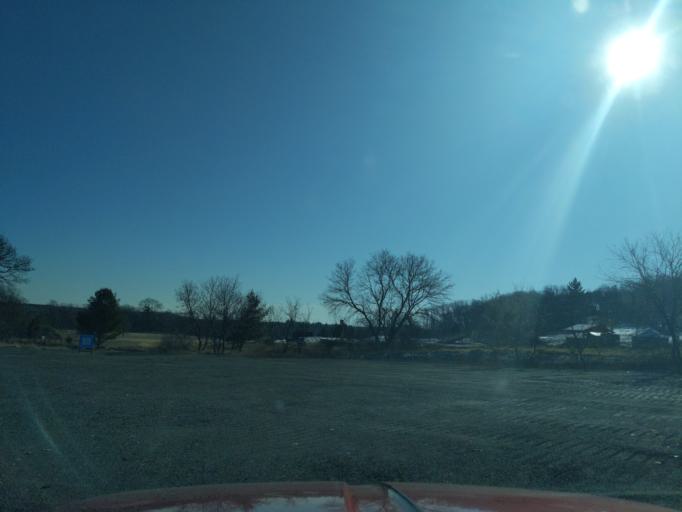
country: US
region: Wisconsin
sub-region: Waushara County
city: Silver Lake
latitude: 44.1216
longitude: -89.1798
